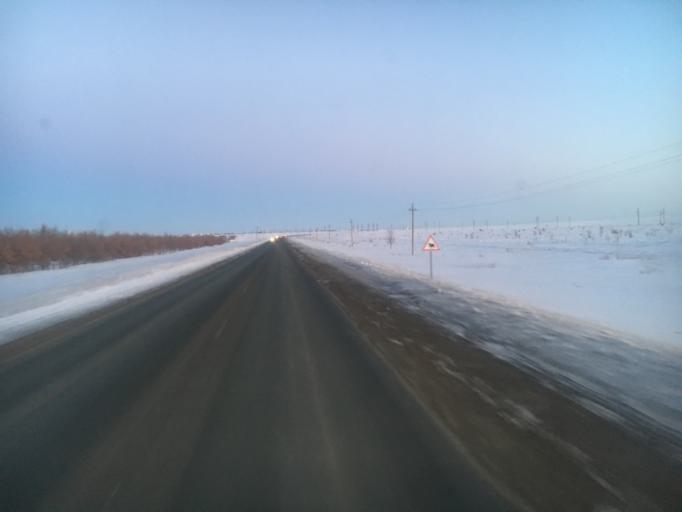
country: KZ
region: Batys Qazaqstan
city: Krugloozernoe
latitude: 51.1489
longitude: 51.3136
